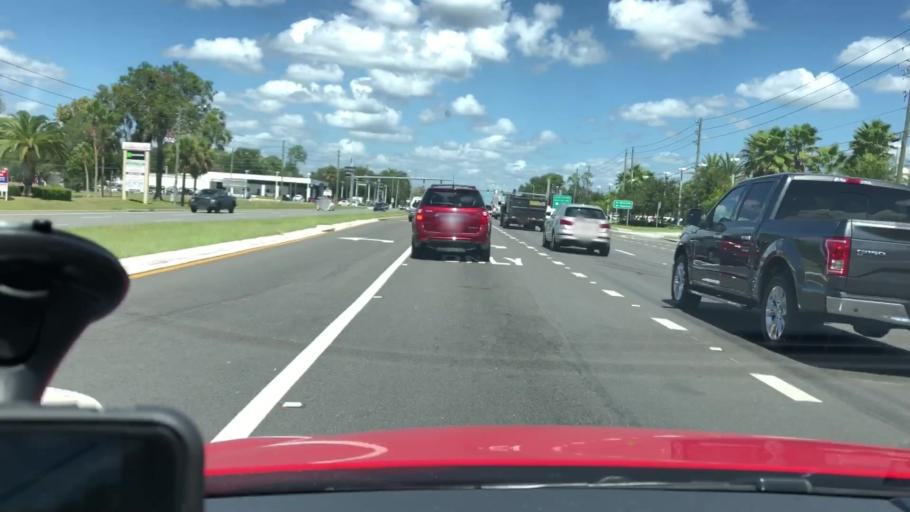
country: US
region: Florida
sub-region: Volusia County
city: De Land Southwest
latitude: 28.9970
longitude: -81.3025
